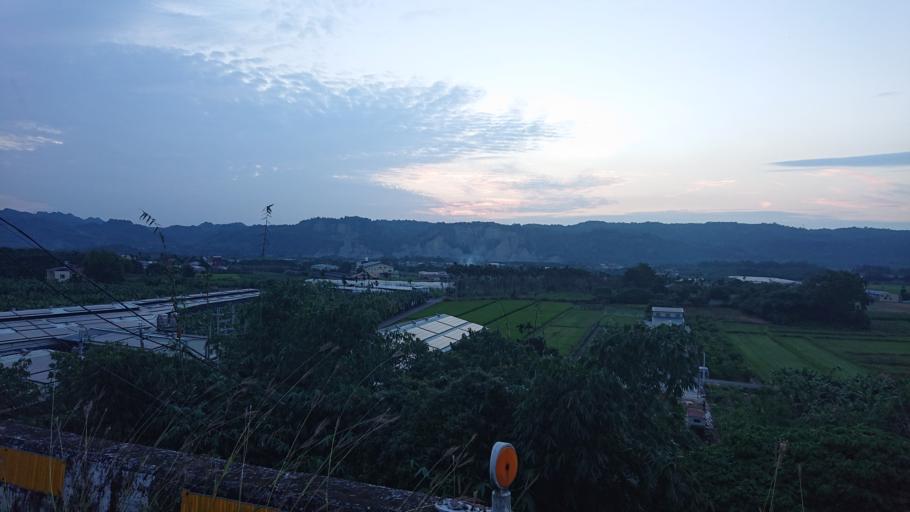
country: TW
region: Taiwan
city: Lugu
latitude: 23.7451
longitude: 120.6739
